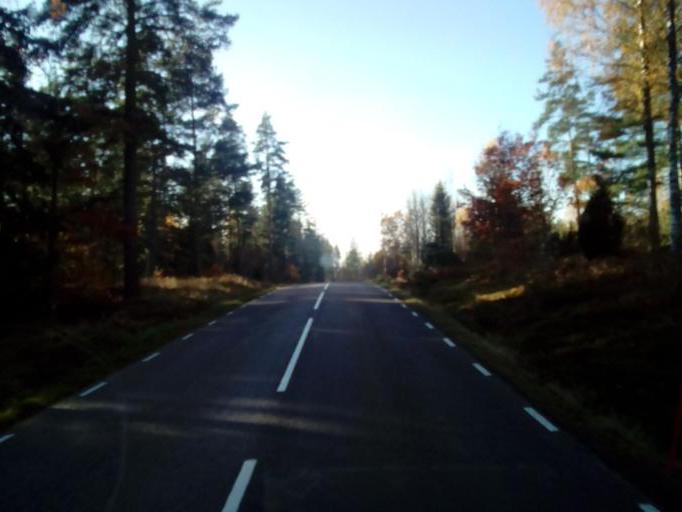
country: SE
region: Kalmar
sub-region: Vasterviks Kommun
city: Ankarsrum
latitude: 57.7740
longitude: 16.1509
